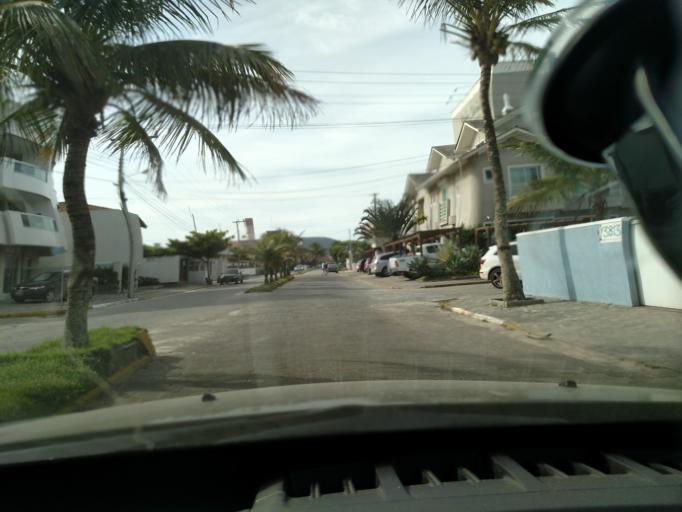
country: BR
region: Santa Catarina
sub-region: Porto Belo
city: Porto Belo
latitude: -27.1929
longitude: -48.4985
